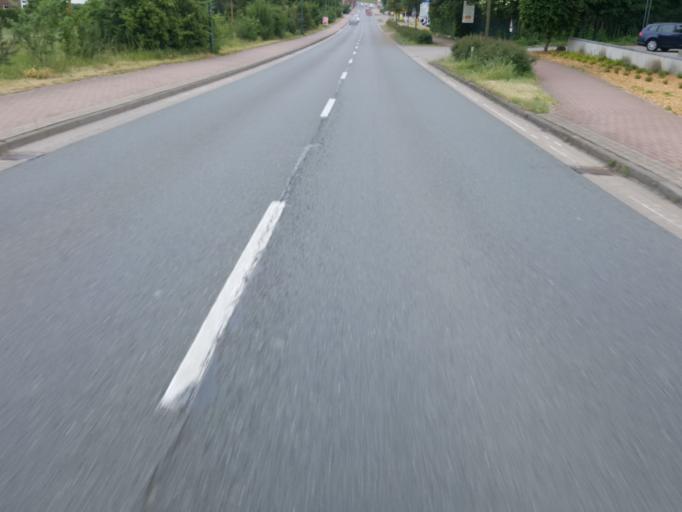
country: DE
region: Lower Saxony
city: Rehburg-Loccum
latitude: 52.4580
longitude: 9.1497
